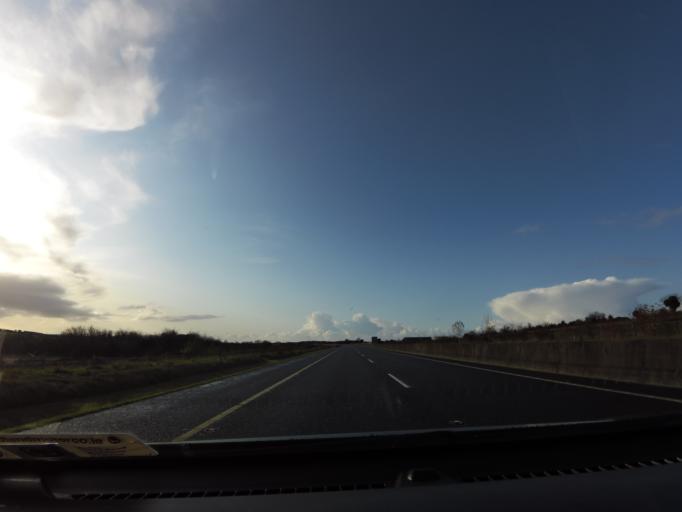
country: IE
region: Connaught
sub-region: County Galway
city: Gort
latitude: 53.0625
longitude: -8.8356
